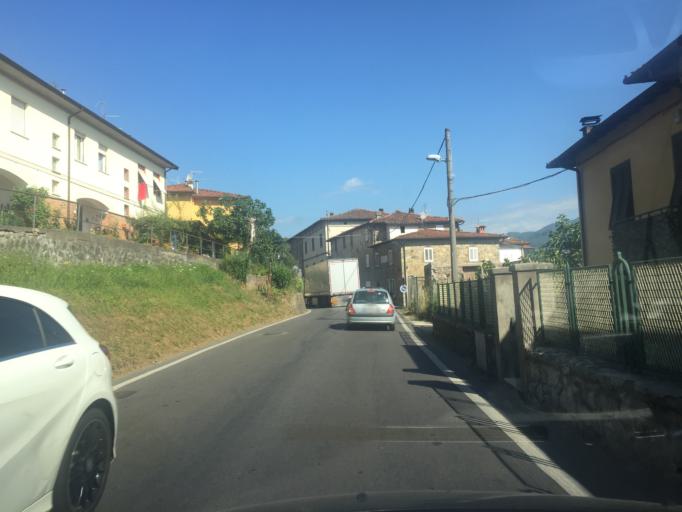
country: IT
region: Tuscany
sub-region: Provincia di Lucca
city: Villa Collemandina
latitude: 44.1333
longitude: 10.3728
